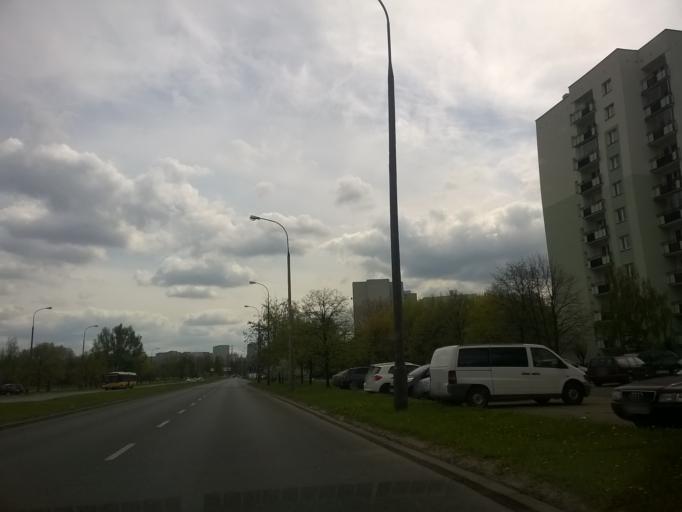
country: PL
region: Masovian Voivodeship
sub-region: Warszawa
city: Ursynow
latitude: 52.1602
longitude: 21.0399
